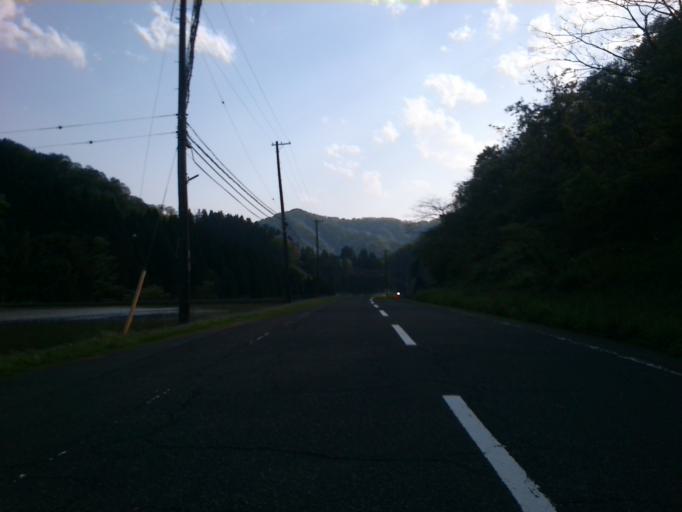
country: JP
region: Kyoto
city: Miyazu
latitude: 35.6913
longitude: 135.1638
